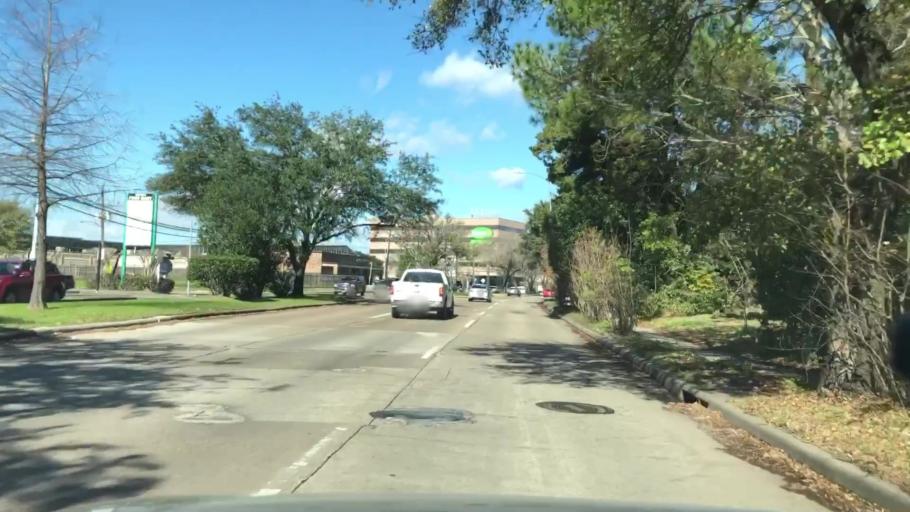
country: US
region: Texas
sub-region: Harris County
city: Bellaire
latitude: 29.6733
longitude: -95.4928
